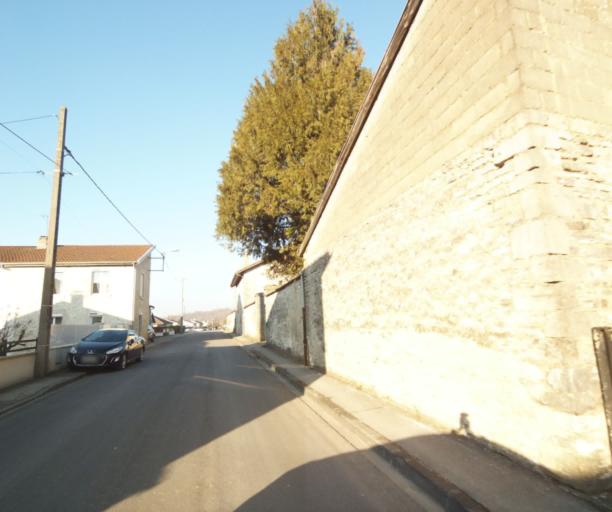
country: FR
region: Champagne-Ardenne
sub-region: Departement de la Haute-Marne
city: Bienville
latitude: 48.5757
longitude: 5.0456
